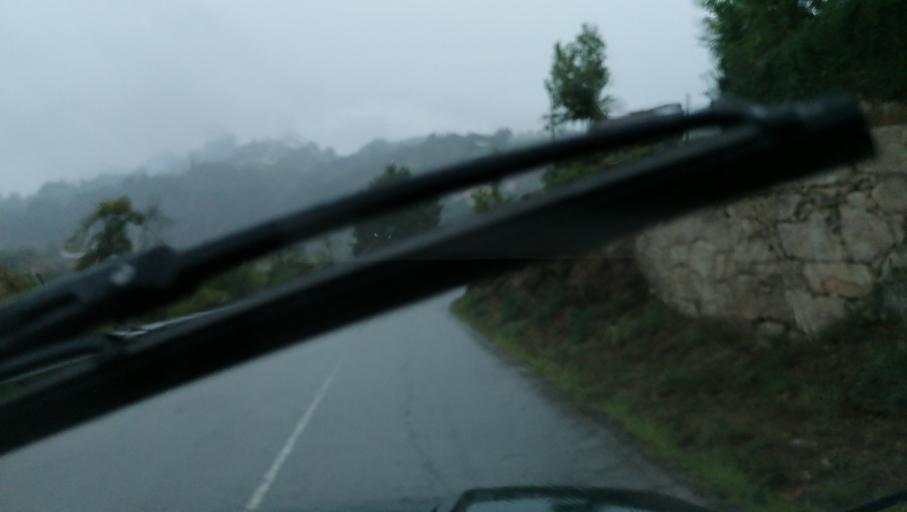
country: PT
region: Braga
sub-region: Cabeceiras de Basto
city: Cabeceiras de Basto
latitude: 41.4885
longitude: -7.9576
